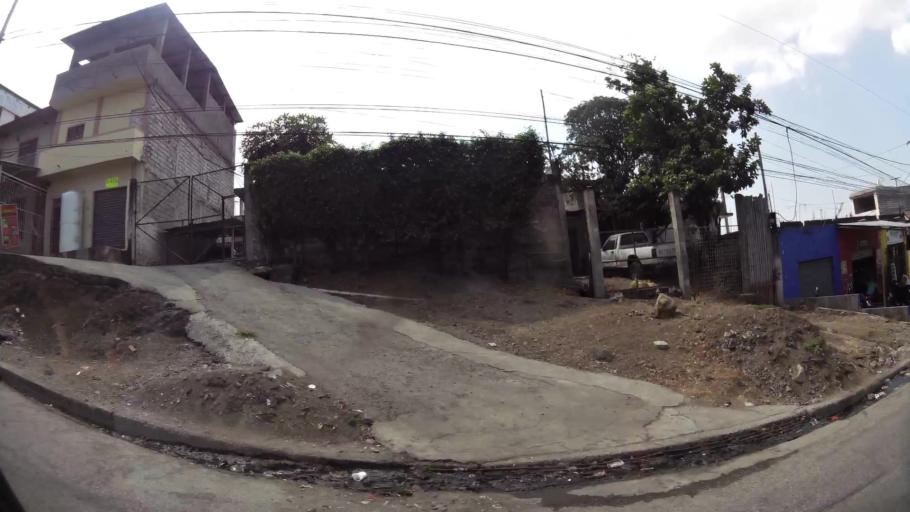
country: EC
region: Guayas
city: Santa Lucia
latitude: -2.1287
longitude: -79.9404
